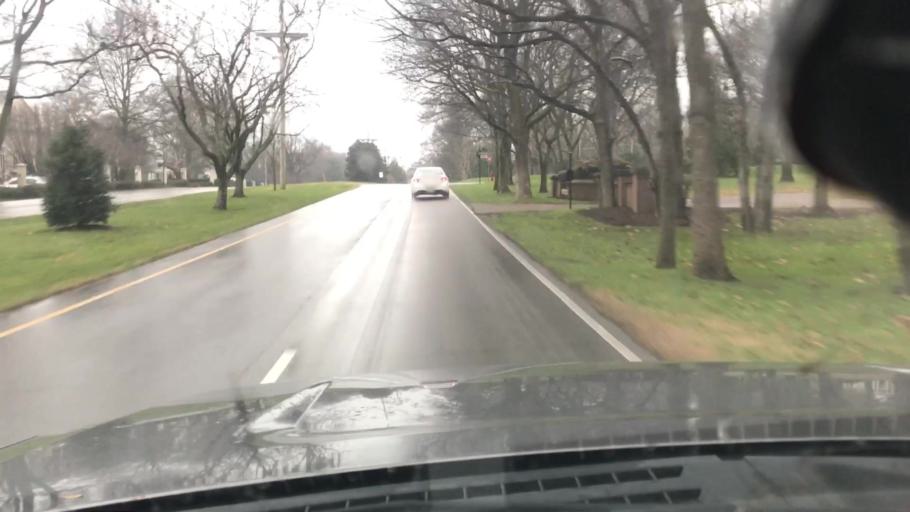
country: US
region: Tennessee
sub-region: Davidson County
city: Belle Meade
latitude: 36.0989
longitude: -86.8567
